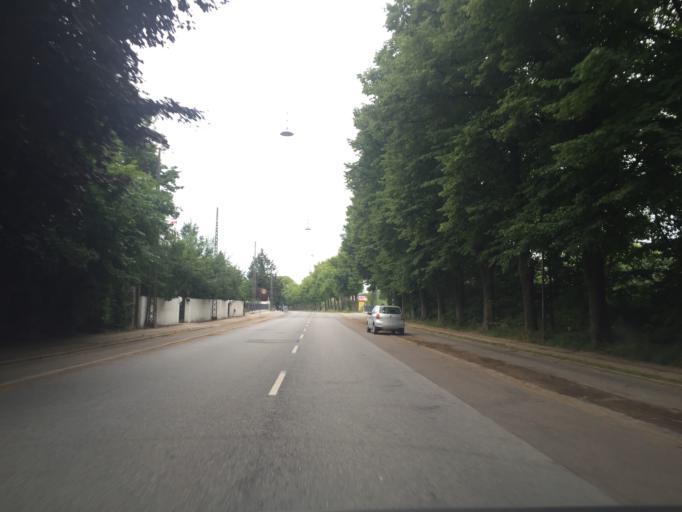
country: DK
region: Capital Region
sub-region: Gentofte Kommune
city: Charlottenlund
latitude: 55.7283
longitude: 12.5687
